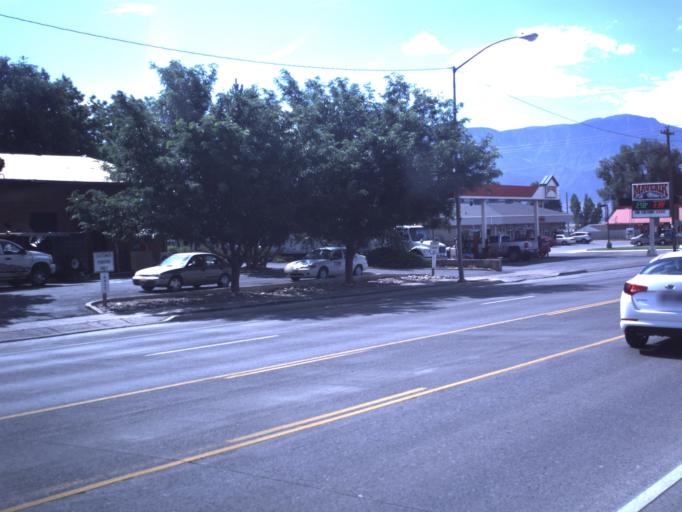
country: US
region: Utah
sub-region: Sevier County
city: Richfield
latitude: 38.7647
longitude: -112.0849
